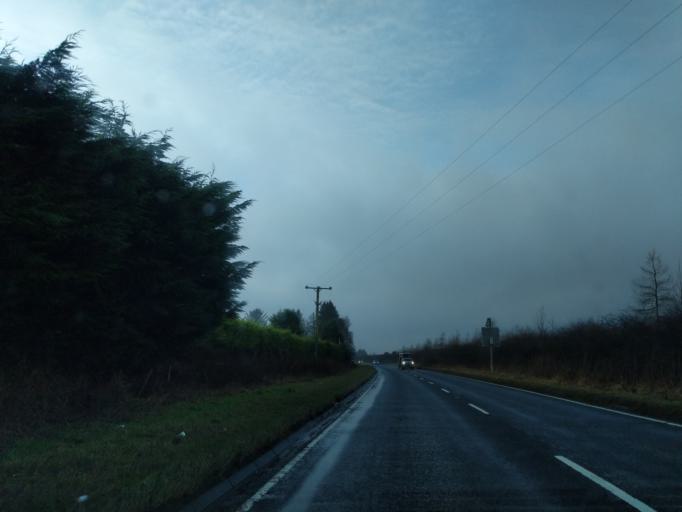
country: GB
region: Scotland
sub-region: Perth and Kinross
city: Kinross
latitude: 56.2080
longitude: -3.4605
